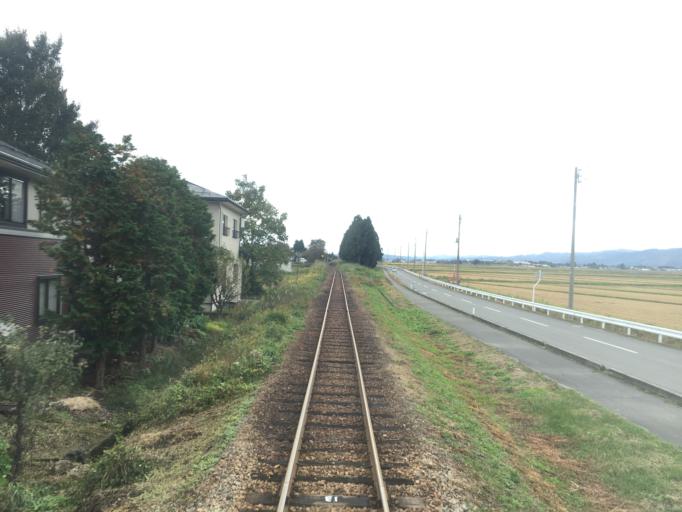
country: JP
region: Yamagata
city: Nagai
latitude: 38.1334
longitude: 140.0358
